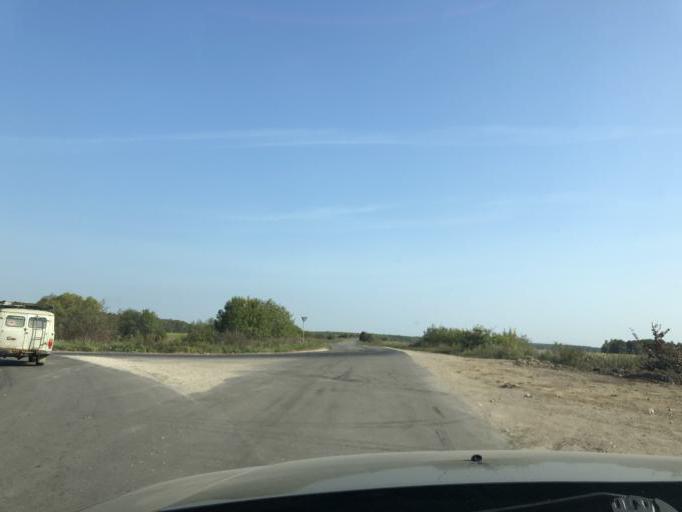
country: RU
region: Tula
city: Novogurovskiy
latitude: 54.4148
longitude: 37.3123
